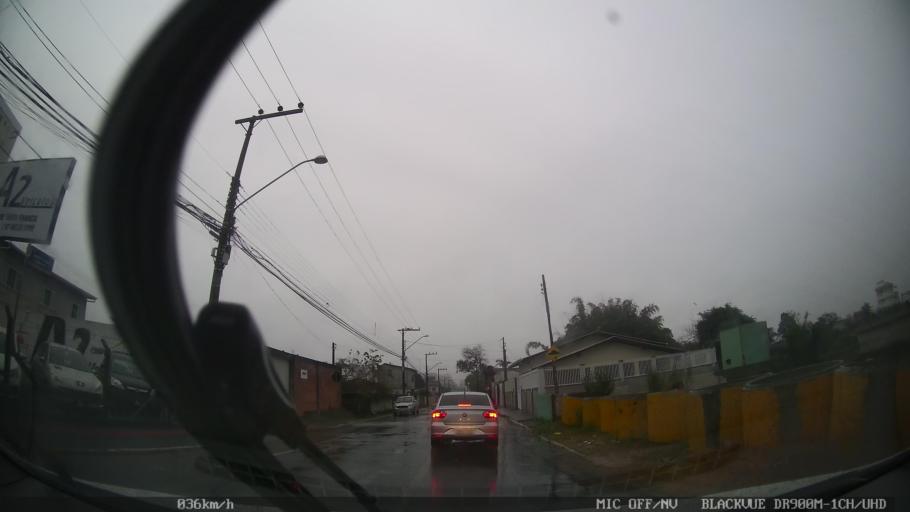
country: BR
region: Santa Catarina
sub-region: Itajai
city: Itajai
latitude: -26.9159
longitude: -48.6831
